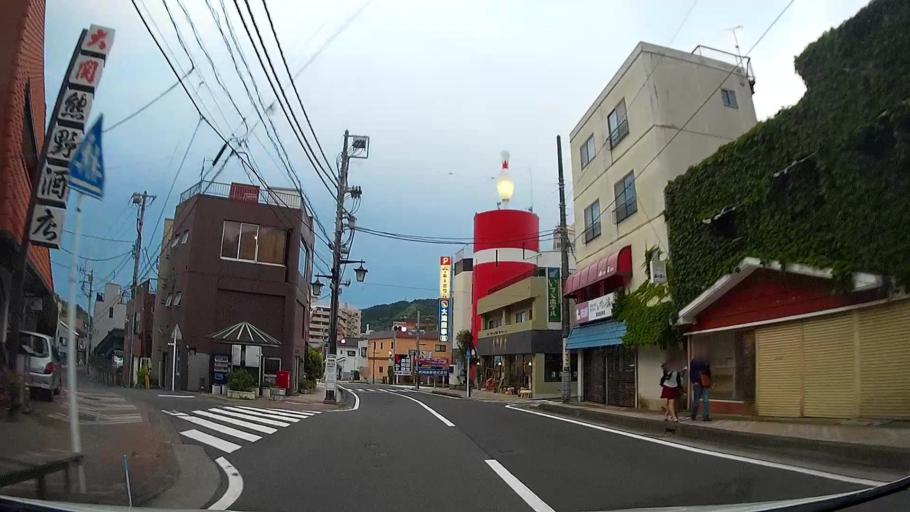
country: JP
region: Kanagawa
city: Yugawara
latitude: 35.1424
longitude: 139.0816
